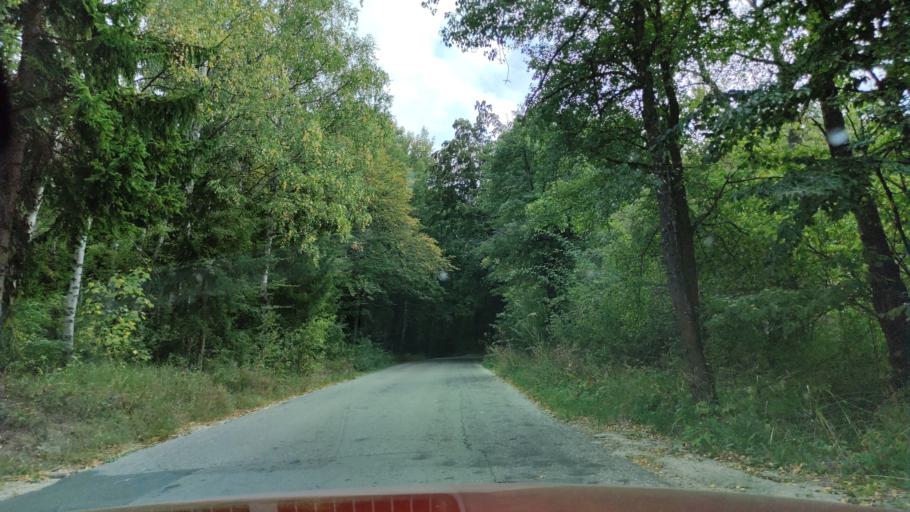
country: BG
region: Sofia-Capital
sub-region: Stolichna Obshtina
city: Sofia
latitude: 42.6270
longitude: 23.2310
